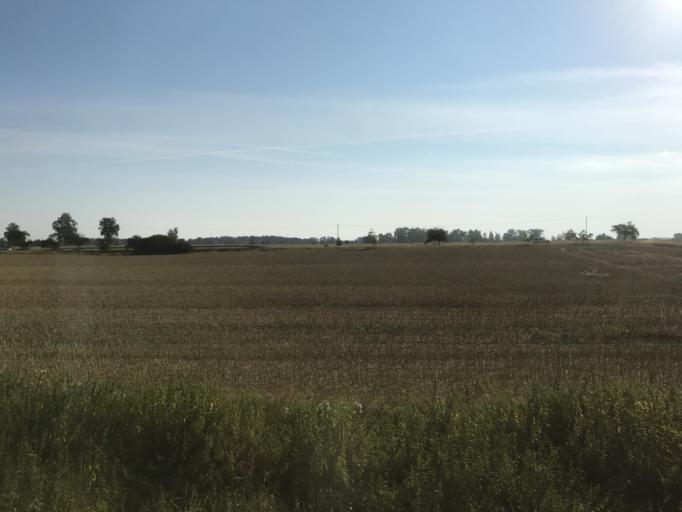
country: CZ
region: Jihocesky
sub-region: Okres Jindrichuv Hradec
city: Lomnice nad Luznici
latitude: 49.0592
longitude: 14.7442
